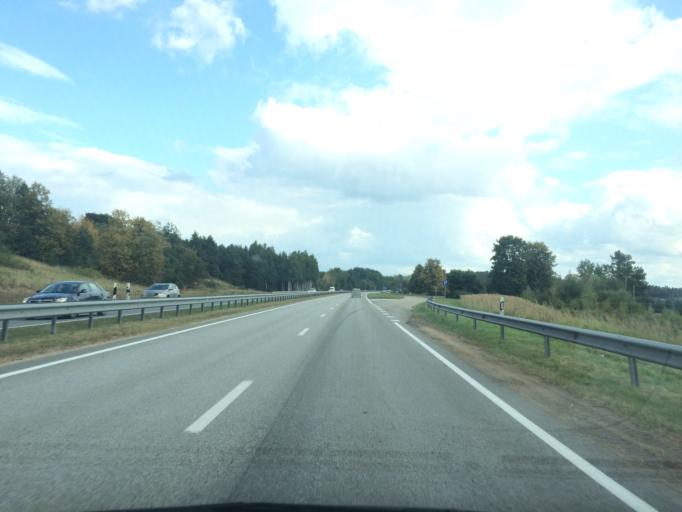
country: LV
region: Ikskile
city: Ikskile
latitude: 56.8453
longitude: 24.4700
